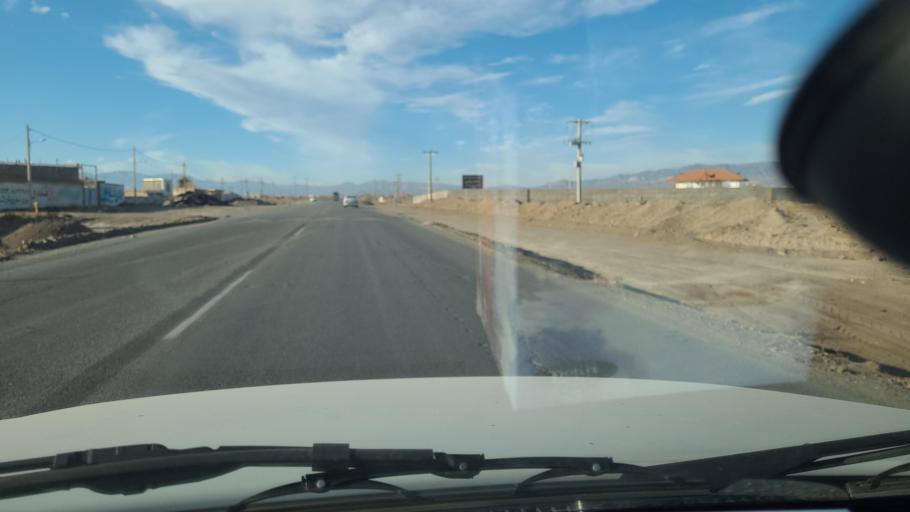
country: IR
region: Razavi Khorasan
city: Sabzevar
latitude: 36.2333
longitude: 57.6467
